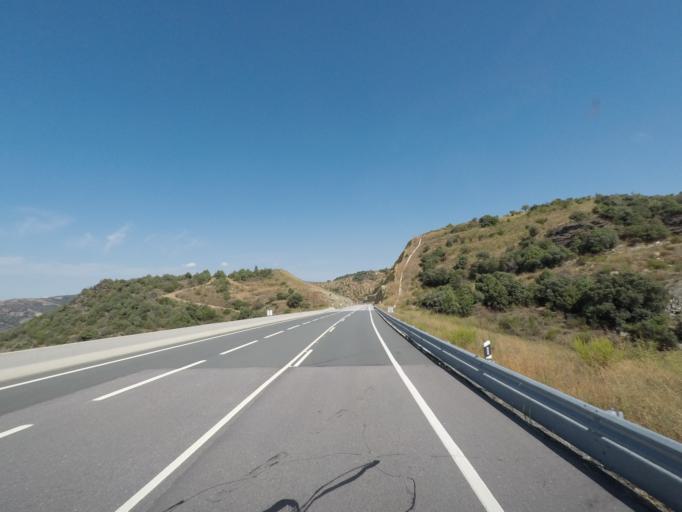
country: PT
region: Braganca
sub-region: Alfandega da Fe
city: Alfandega da Fe
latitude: 41.2898
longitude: -6.8957
